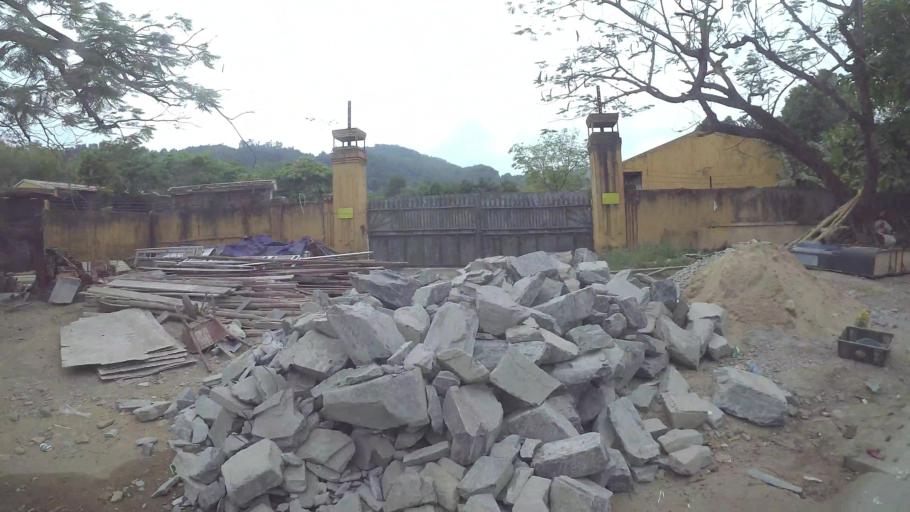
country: VN
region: Da Nang
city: Cam Le
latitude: 16.0335
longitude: 108.1788
